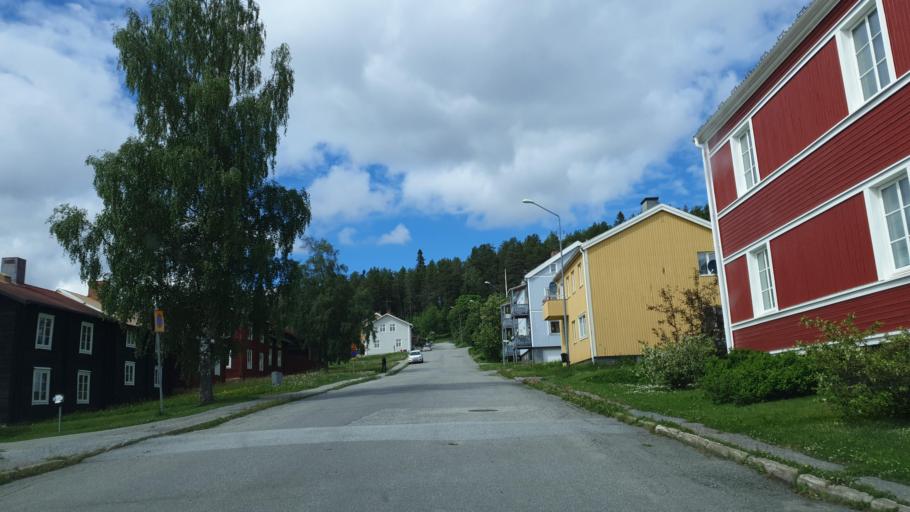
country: SE
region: Vaesterbotten
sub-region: Vilhelmina Kommun
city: Vilhelmina
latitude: 64.6282
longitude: 16.6516
